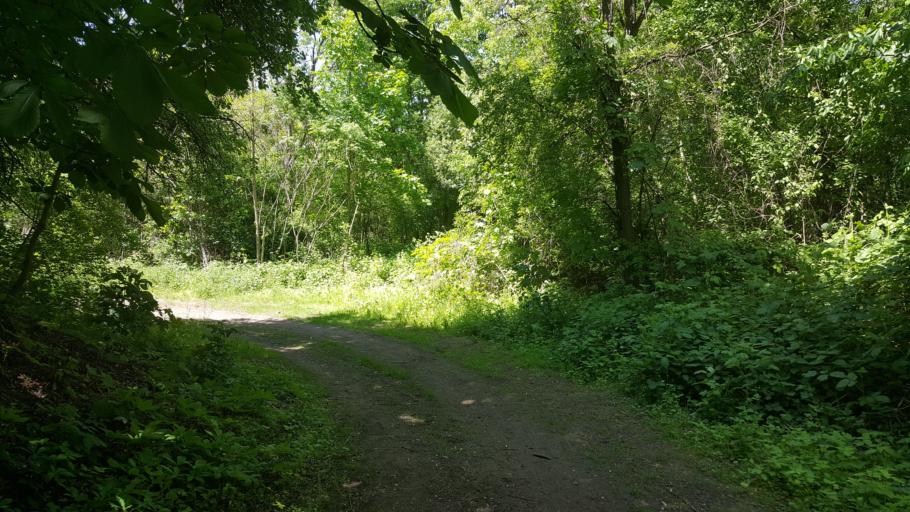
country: DE
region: Saxony
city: Albertstadt
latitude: 51.0933
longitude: 13.7528
